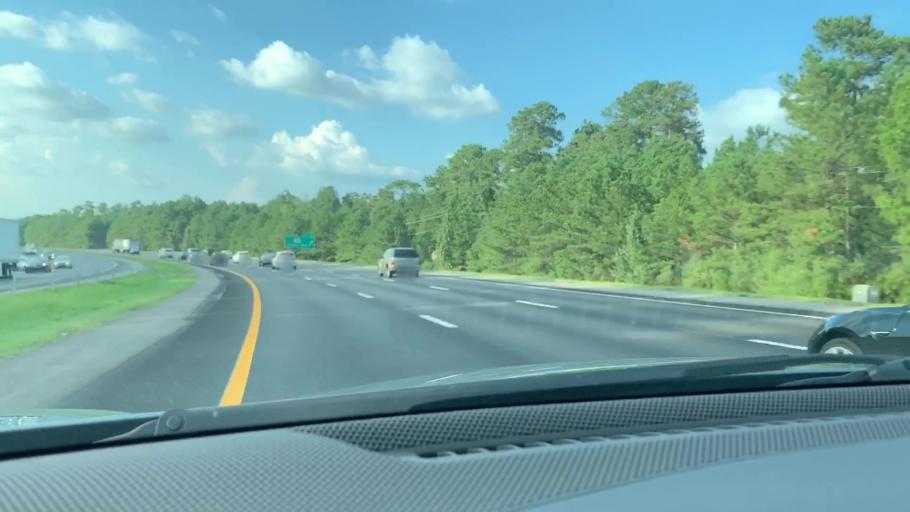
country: US
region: South Carolina
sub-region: Richland County
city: Forest Acres
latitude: 33.9893
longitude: -80.9530
